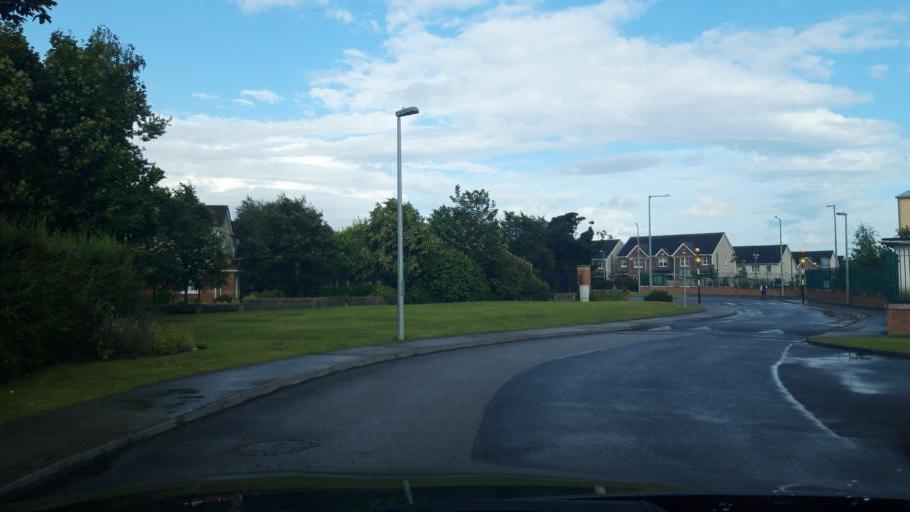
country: IE
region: Leinster
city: Hartstown
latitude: 53.3987
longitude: -6.4358
